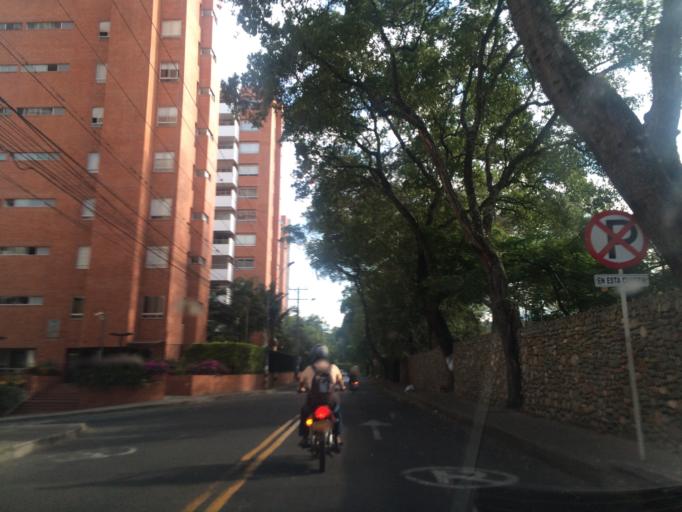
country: CO
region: Valle del Cauca
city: Cali
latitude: 3.3717
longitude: -76.5409
